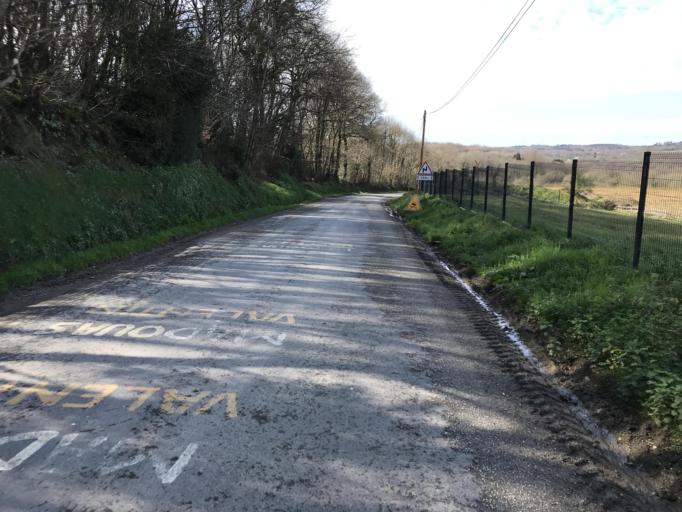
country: FR
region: Brittany
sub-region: Departement du Finistere
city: Loperhet
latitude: 48.3764
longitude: -4.2888
